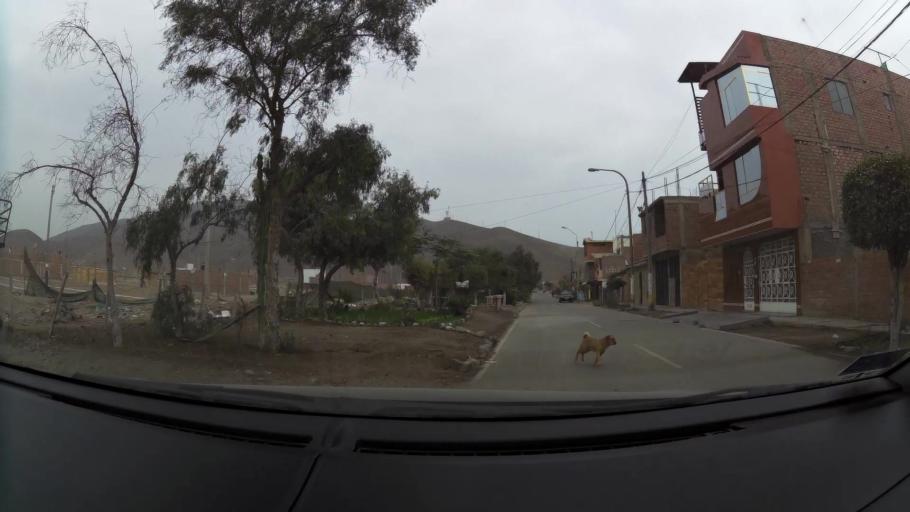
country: PE
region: Lima
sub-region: Lima
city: Santa Rosa
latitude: -11.7893
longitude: -77.1509
